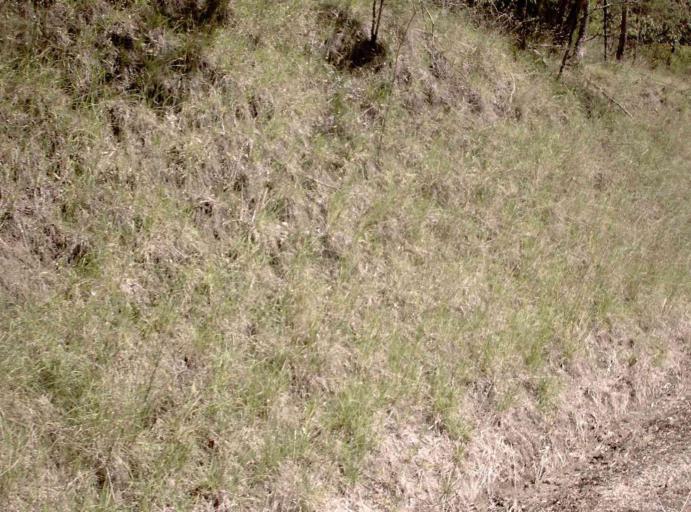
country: AU
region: Victoria
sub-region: East Gippsland
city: Lakes Entrance
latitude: -37.3448
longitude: 148.2298
